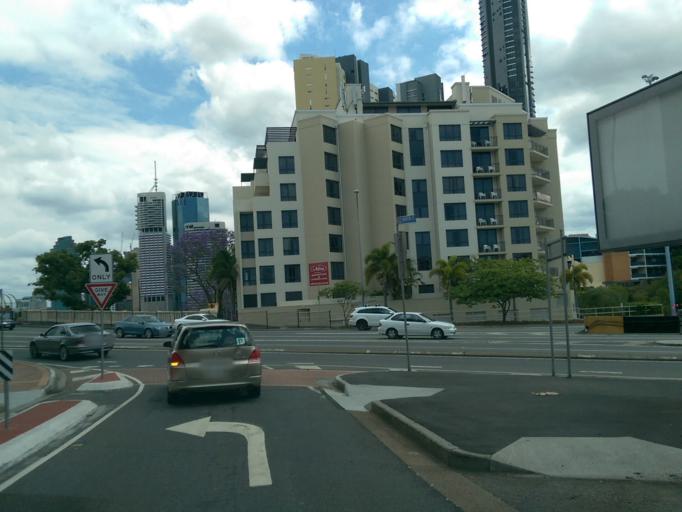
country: AU
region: Queensland
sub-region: Brisbane
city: Fortitude Valley
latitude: -27.4610
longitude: 153.0359
